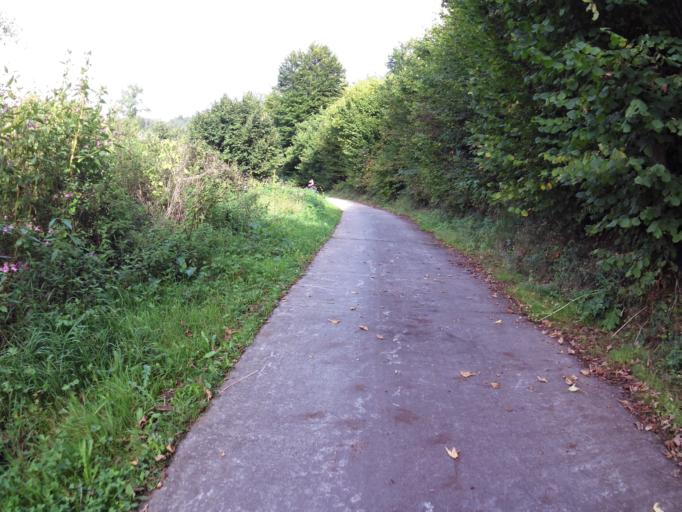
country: DE
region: Baden-Wuerttemberg
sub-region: Freiburg Region
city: Villingendorf
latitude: 48.2039
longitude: 8.6105
